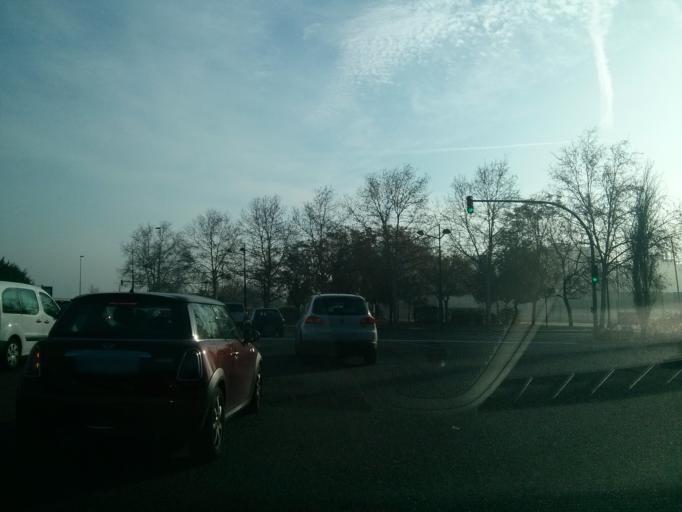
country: ES
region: Valencia
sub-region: Provincia de Valencia
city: Tavernes Blanques
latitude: 39.4973
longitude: -0.3852
